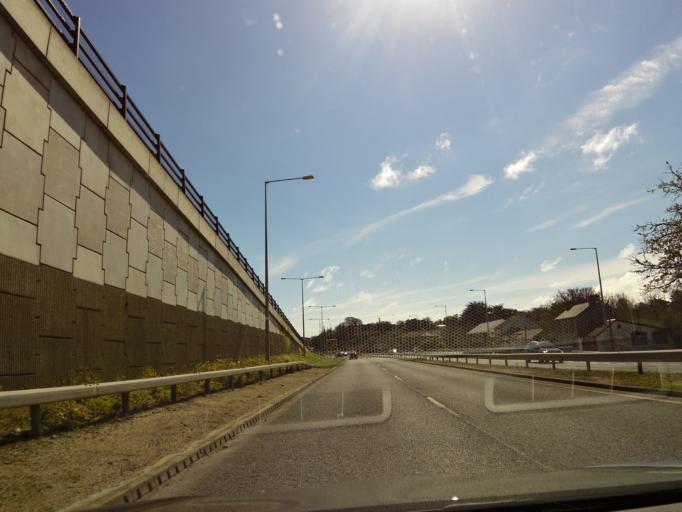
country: IE
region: Leinster
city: Loughlinstown
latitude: 53.2468
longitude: -6.1363
